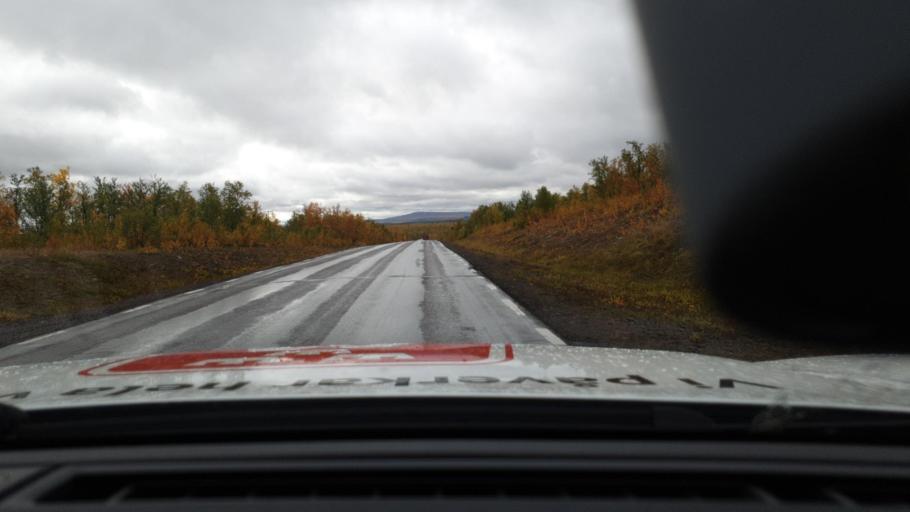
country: SE
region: Norrbotten
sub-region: Kiruna Kommun
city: Kiruna
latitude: 67.7938
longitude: 20.2317
